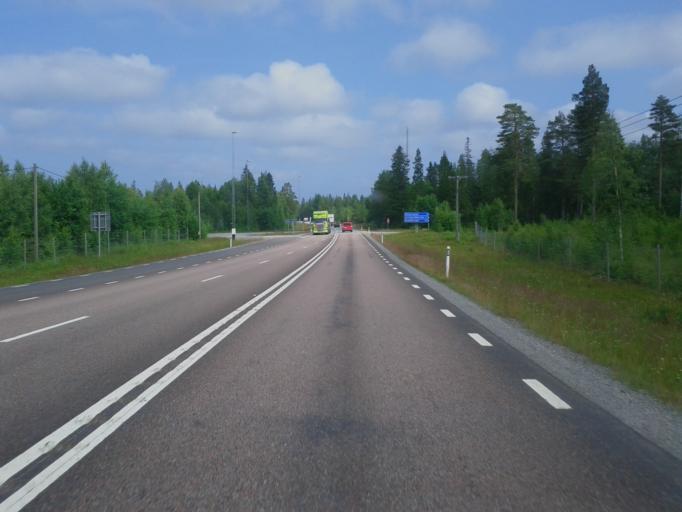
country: SE
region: Vaesterbotten
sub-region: Skelleftea Kommun
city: Burea
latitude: 64.4639
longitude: 21.2922
